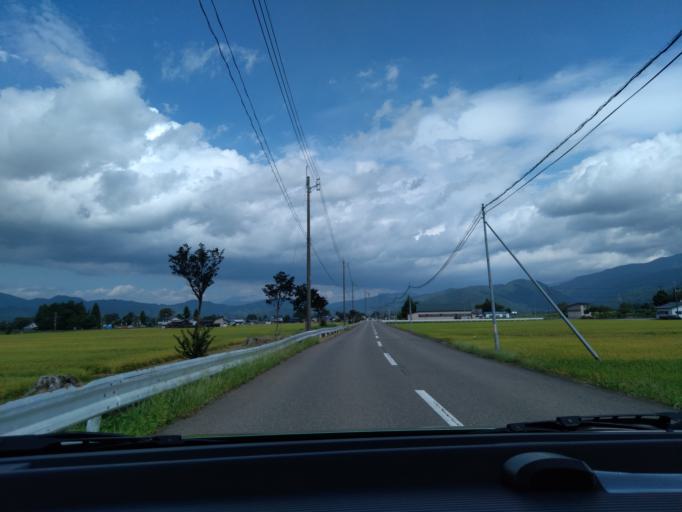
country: JP
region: Akita
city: Kakunodatemachi
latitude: 39.6018
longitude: 140.5836
